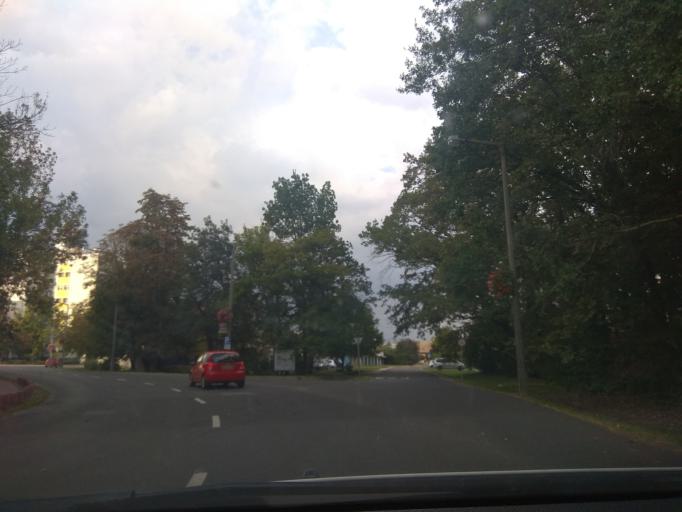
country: HU
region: Borsod-Abauj-Zemplen
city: Sajooeroes
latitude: 47.9262
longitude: 21.0431
